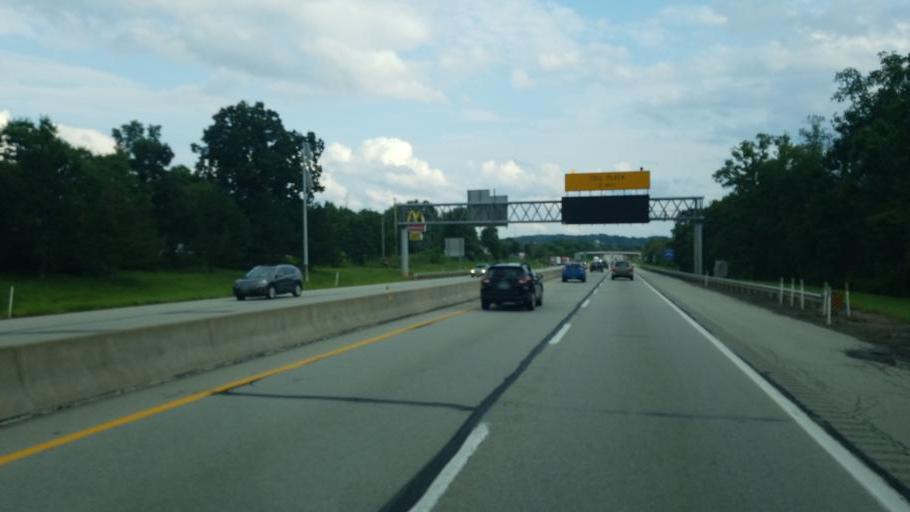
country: US
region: Pennsylvania
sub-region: Butler County
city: Cranberry Township
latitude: 40.6731
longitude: -80.1011
